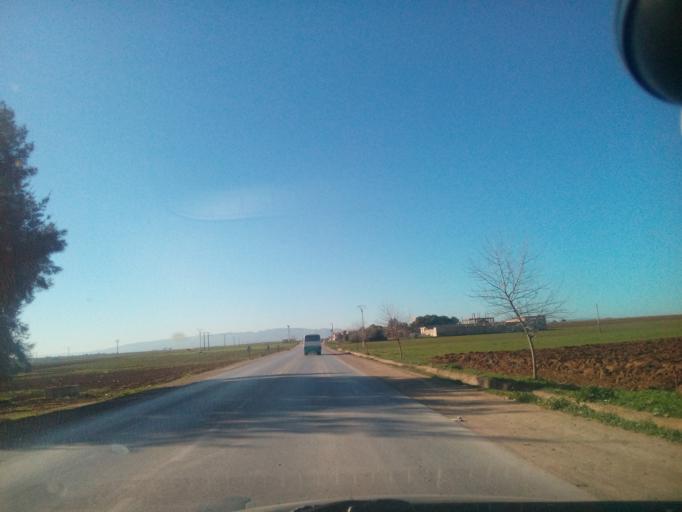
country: DZ
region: Relizane
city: Djidiouia
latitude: 35.8947
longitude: 0.6638
